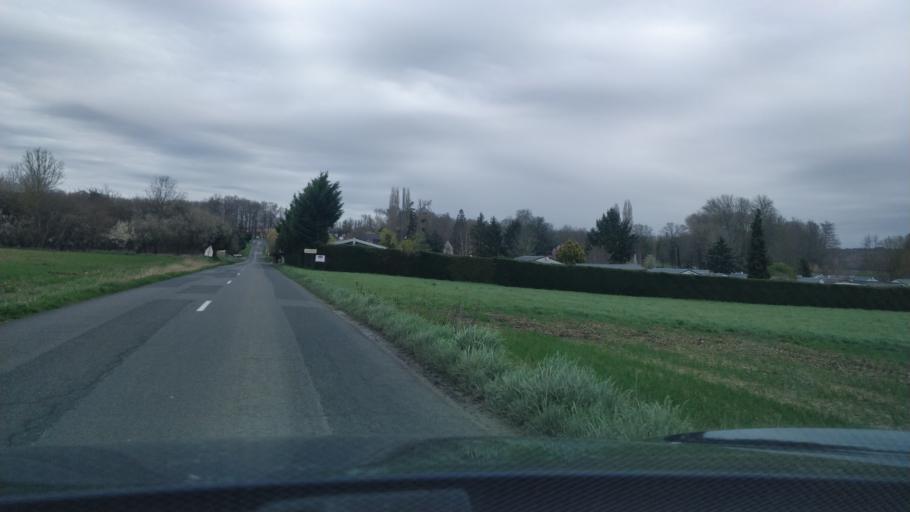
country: FR
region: Ile-de-France
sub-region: Departement de l'Essonne
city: Saint-Maurice-Montcouronne
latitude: 48.5881
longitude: 2.1082
